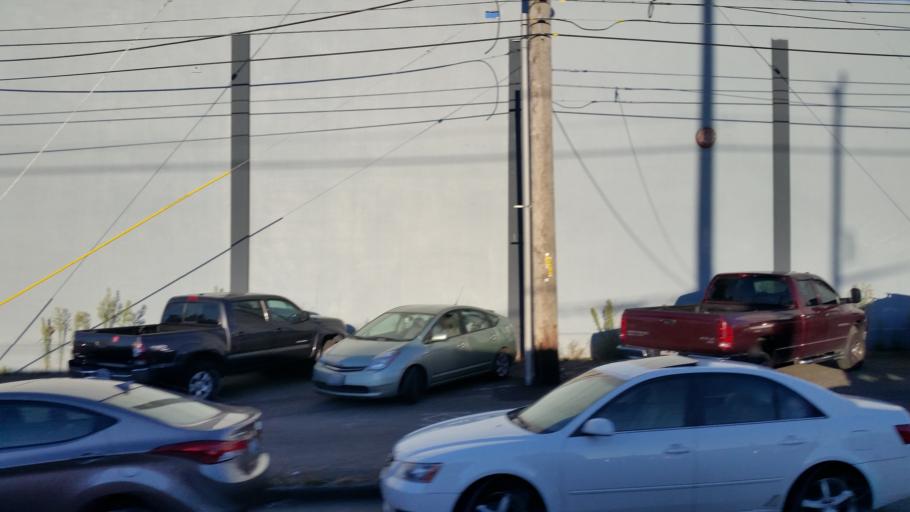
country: US
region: Washington
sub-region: King County
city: Seattle
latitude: 47.5815
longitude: -122.3260
